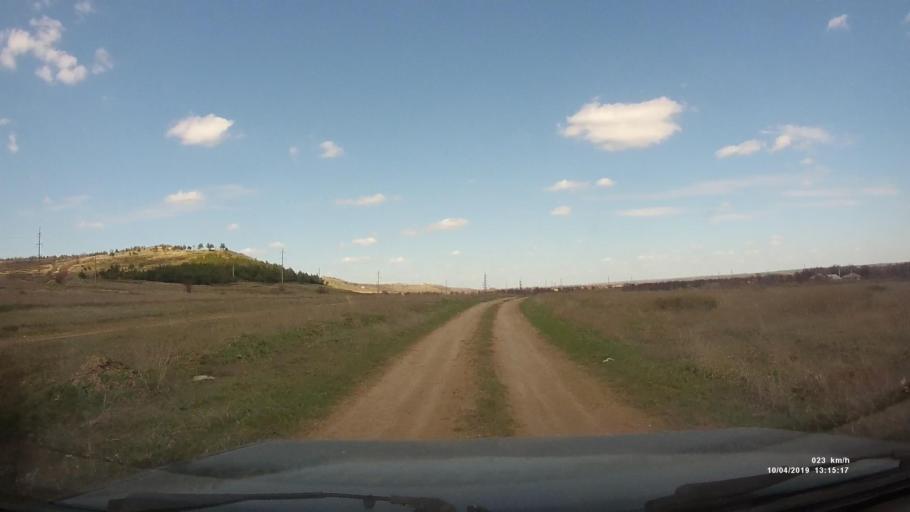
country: RU
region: Rostov
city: Masalovka
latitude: 48.4171
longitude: 40.2589
